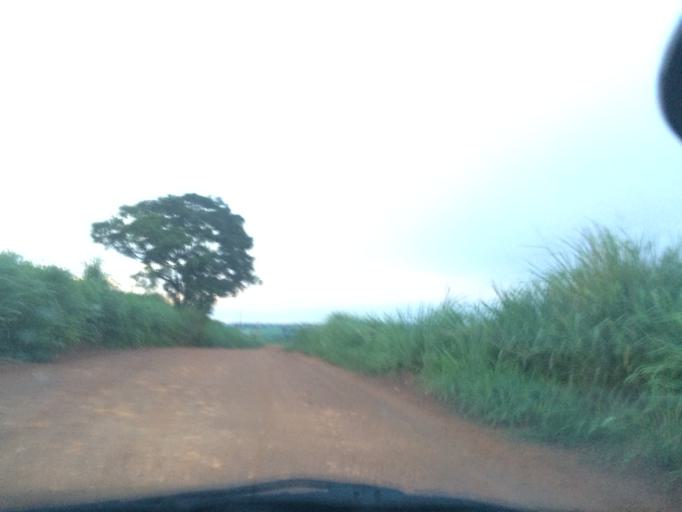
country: BR
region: Sao Paulo
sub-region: Tambau
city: Tambau
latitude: -21.7015
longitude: -47.2138
